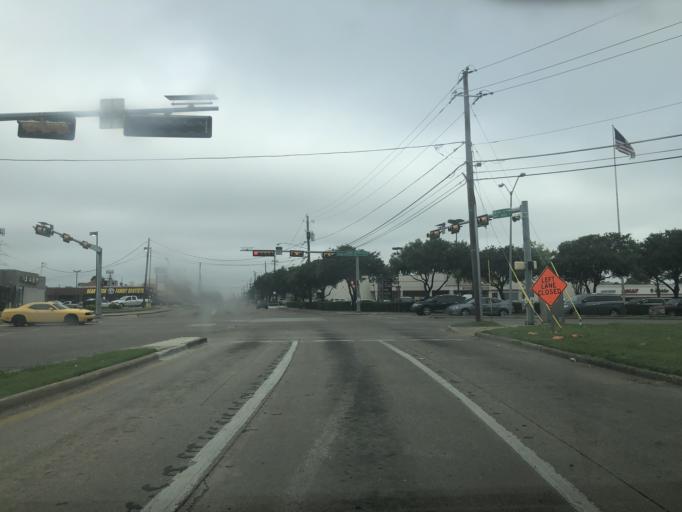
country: US
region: Texas
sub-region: Dallas County
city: University Park
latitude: 32.8664
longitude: -96.8643
